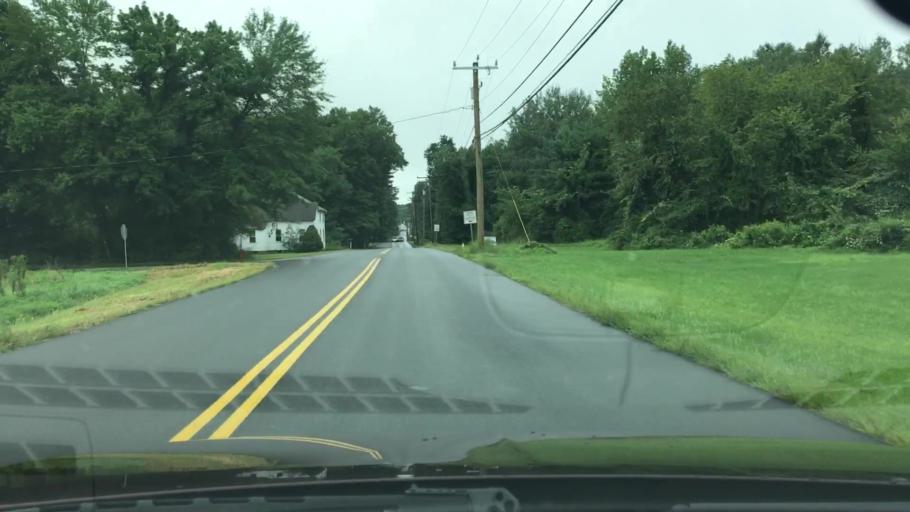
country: US
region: Connecticut
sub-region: Hartford County
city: Tariffville
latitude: 41.9138
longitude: -72.7824
